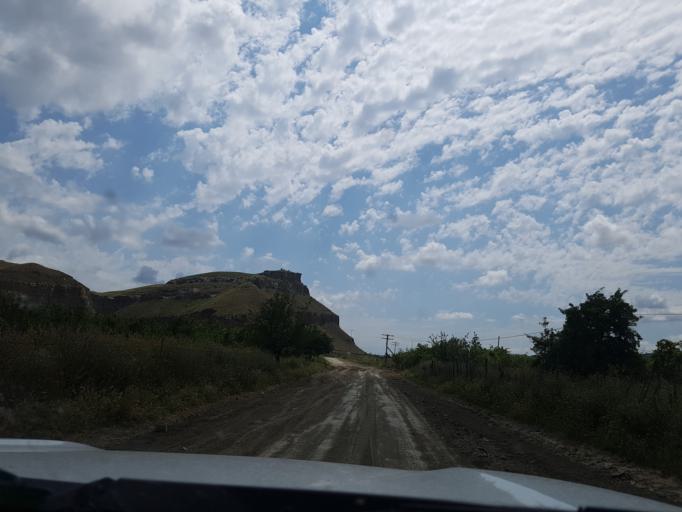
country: TM
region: Ahal
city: Baharly
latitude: 38.2229
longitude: 56.8959
